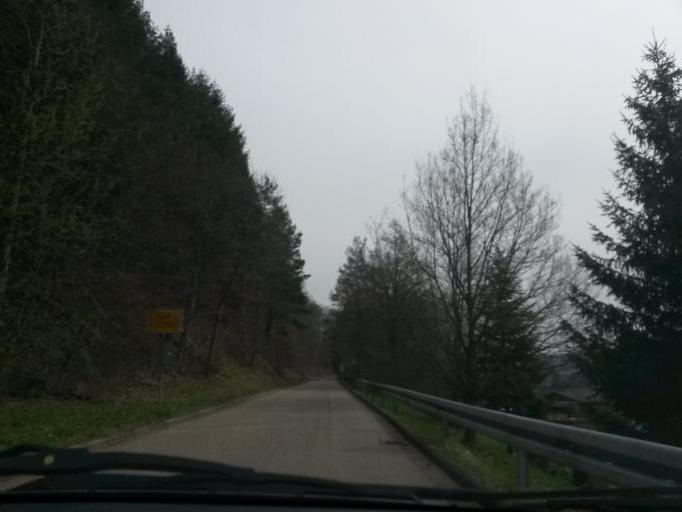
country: DE
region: Baden-Wuerttemberg
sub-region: Freiburg Region
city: Lahr
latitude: 48.3100
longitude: 7.8641
